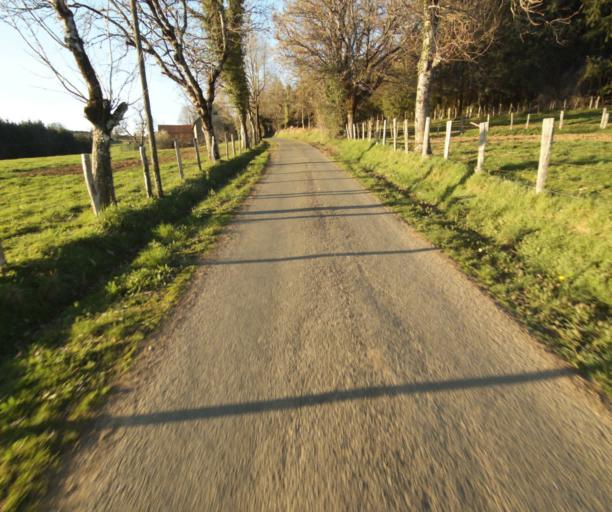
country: FR
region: Limousin
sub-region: Departement de la Correze
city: Saint-Clement
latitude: 45.3367
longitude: 1.7136
